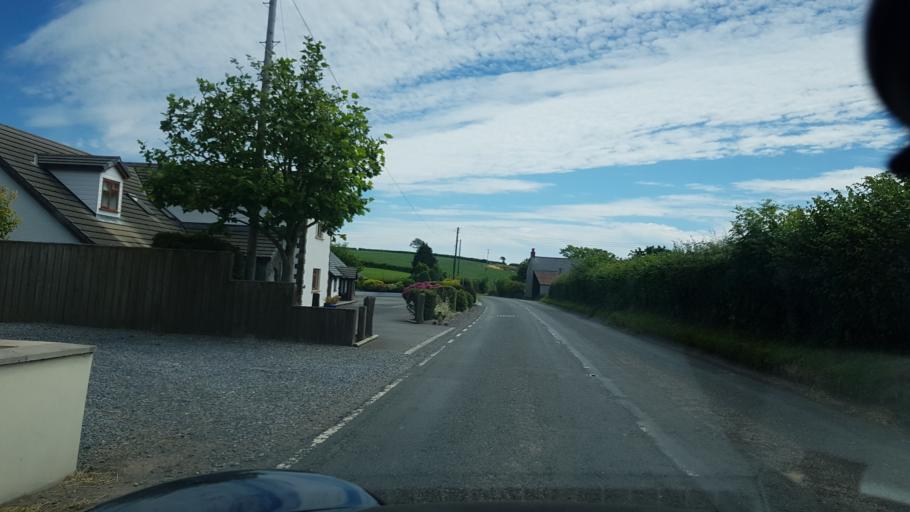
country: GB
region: Wales
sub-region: Carmarthenshire
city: Saint Clears
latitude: 51.7838
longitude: -4.4743
